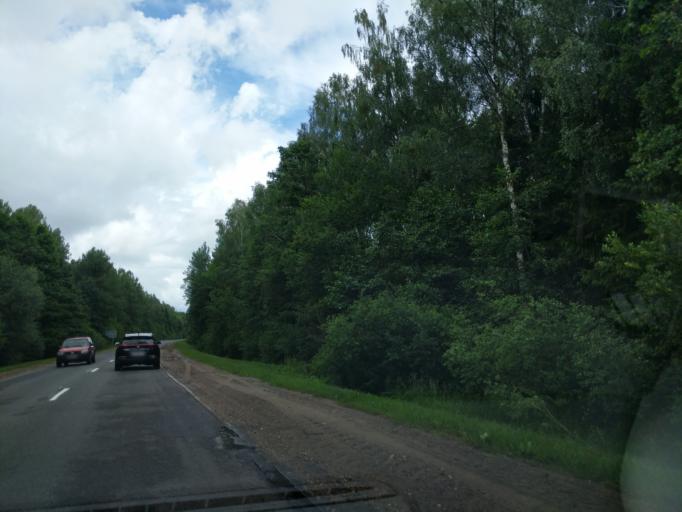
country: BY
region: Minsk
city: Il'ya
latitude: 54.4147
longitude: 27.2638
